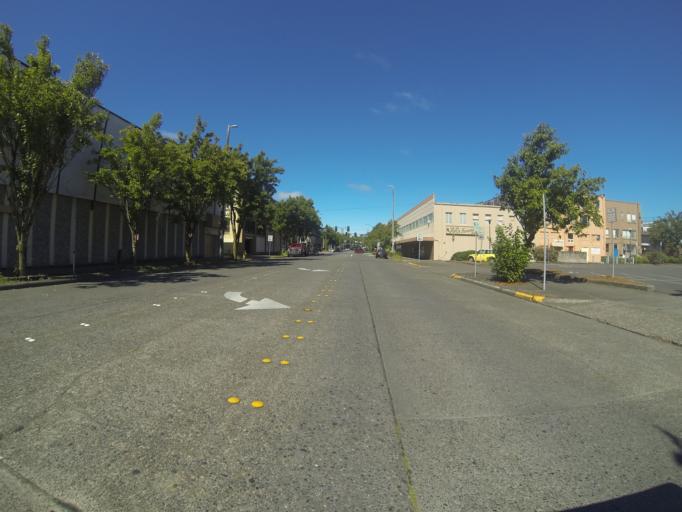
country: US
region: Washington
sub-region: Cowlitz County
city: Longview
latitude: 46.1368
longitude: -122.9335
